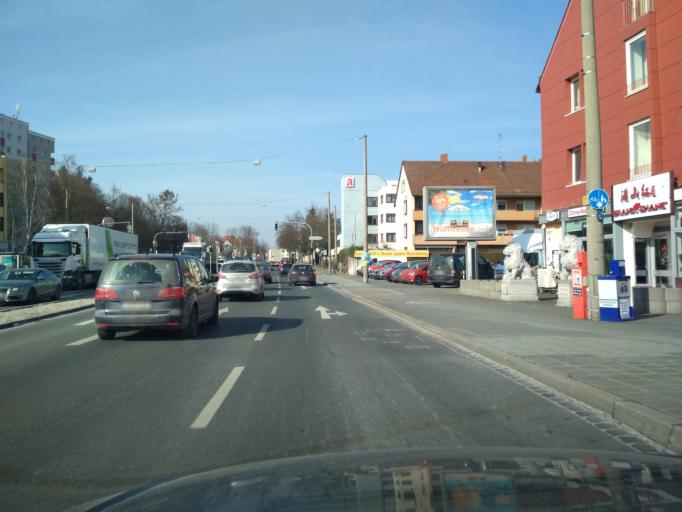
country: DE
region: Bavaria
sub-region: Regierungsbezirk Mittelfranken
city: Stein
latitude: 49.4085
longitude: 11.0354
